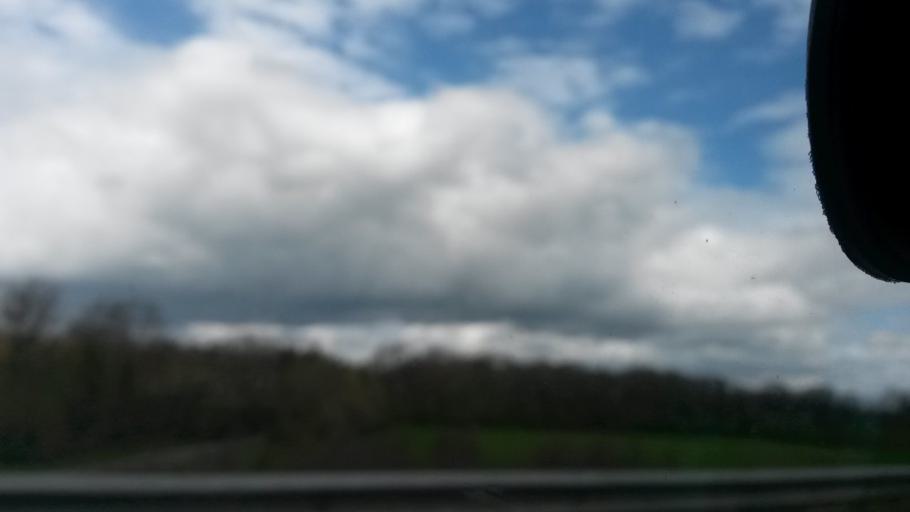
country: IE
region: Leinster
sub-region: Laois
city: Mountrath
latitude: 52.9407
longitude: -7.4533
